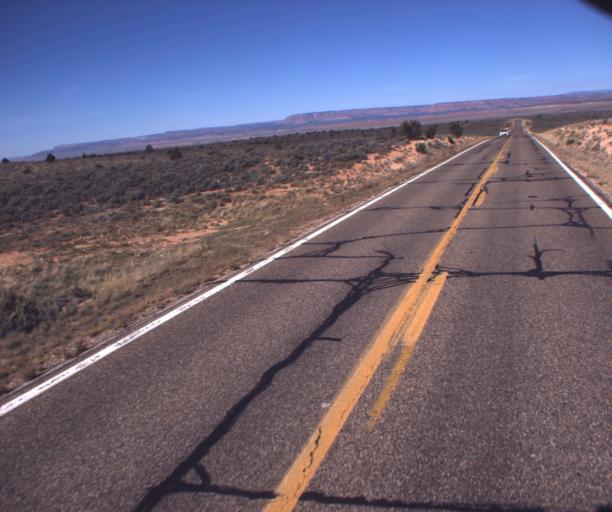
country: US
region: Arizona
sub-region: Coconino County
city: Fredonia
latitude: 36.8799
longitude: -112.3381
